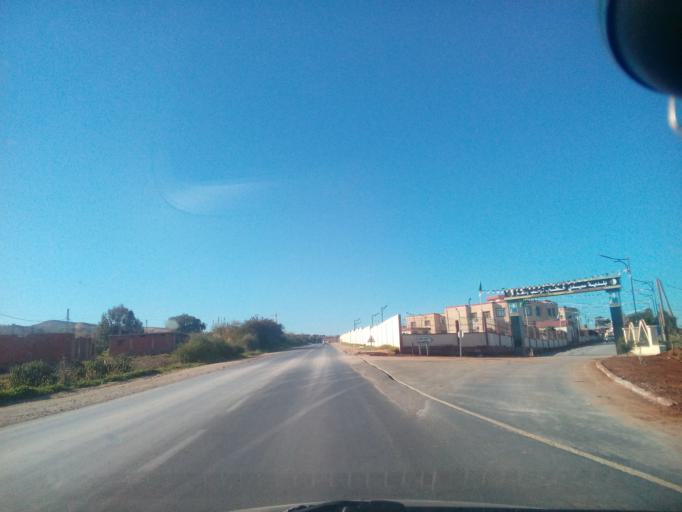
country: DZ
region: Relizane
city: Relizane
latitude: 35.9041
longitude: 0.5177
